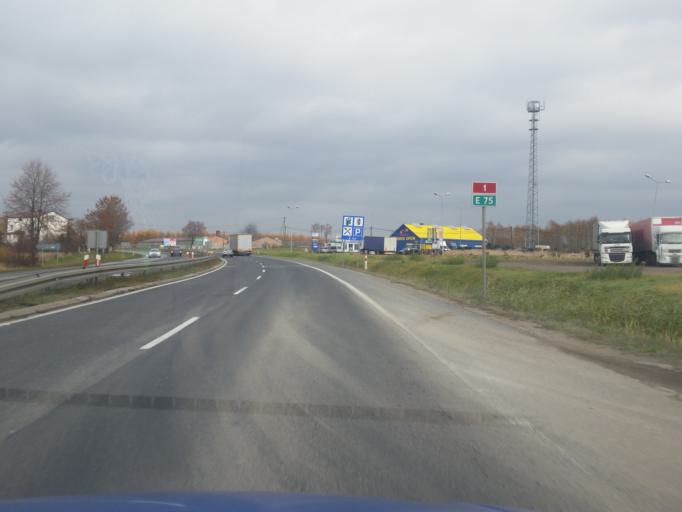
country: PL
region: Silesian Voivodeship
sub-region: Powiat myszkowski
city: Kozieglowy
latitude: 50.6061
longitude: 19.1545
